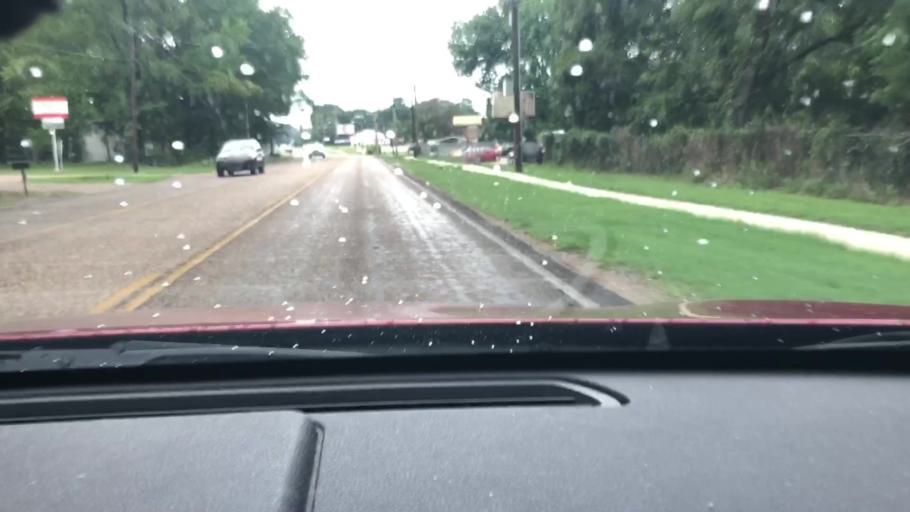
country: US
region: Texas
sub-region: Bowie County
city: Nash
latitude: 33.4428
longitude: -94.1204
